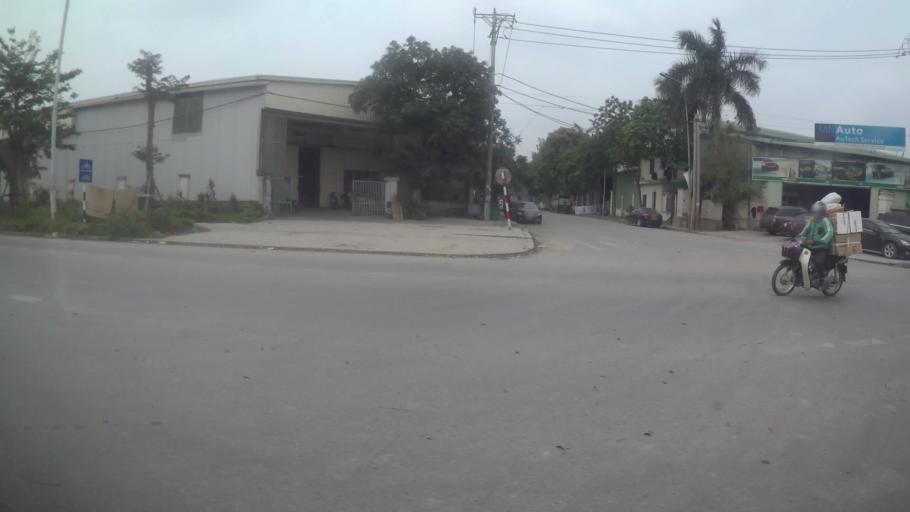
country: VN
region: Ha Noi
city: Cau Dien
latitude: 21.0405
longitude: 105.7397
